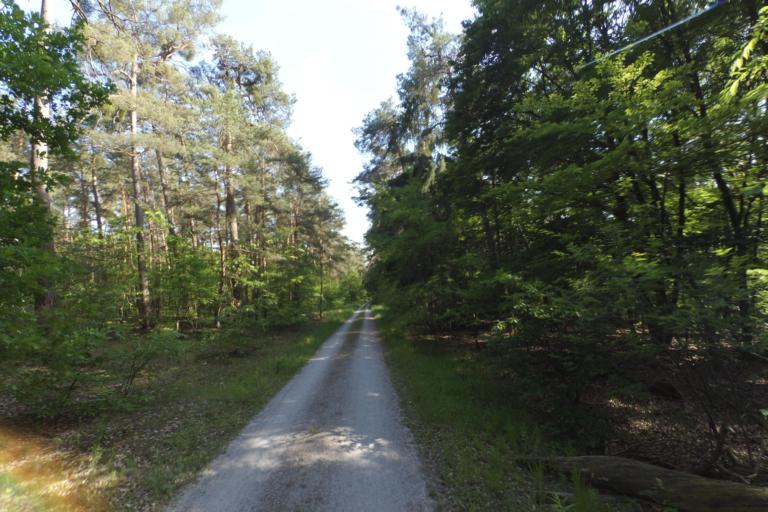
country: DE
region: Hesse
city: Viernheim
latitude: 49.5735
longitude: 8.5347
